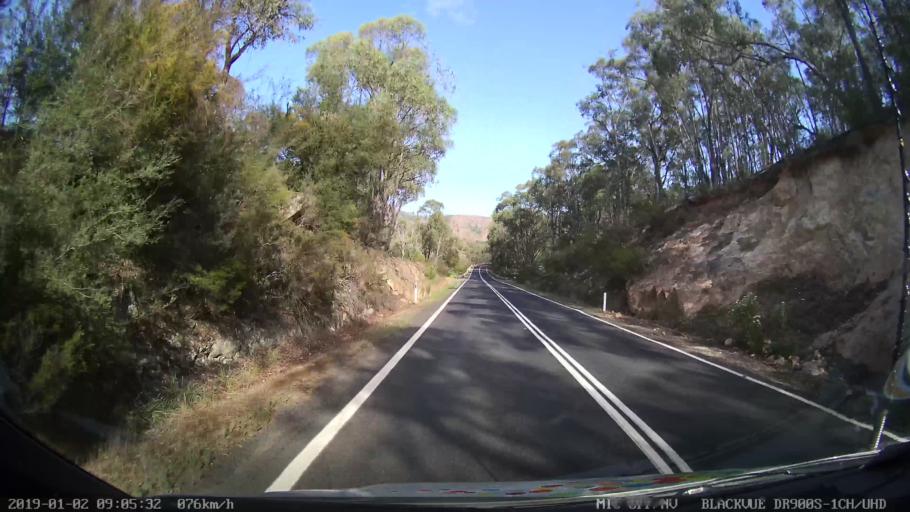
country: AU
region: New South Wales
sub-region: Tumut Shire
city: Tumut
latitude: -35.5601
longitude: 148.3080
